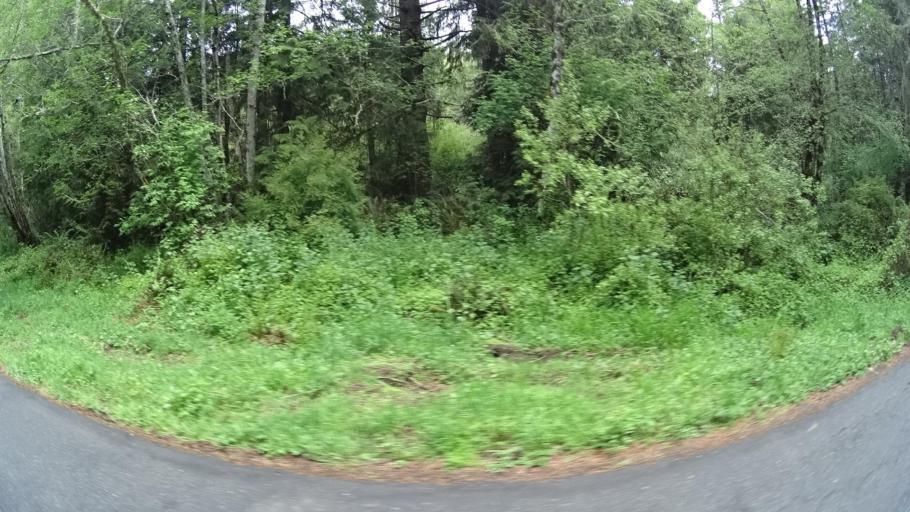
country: US
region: California
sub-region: Humboldt County
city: Bayside
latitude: 40.8286
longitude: -124.0114
